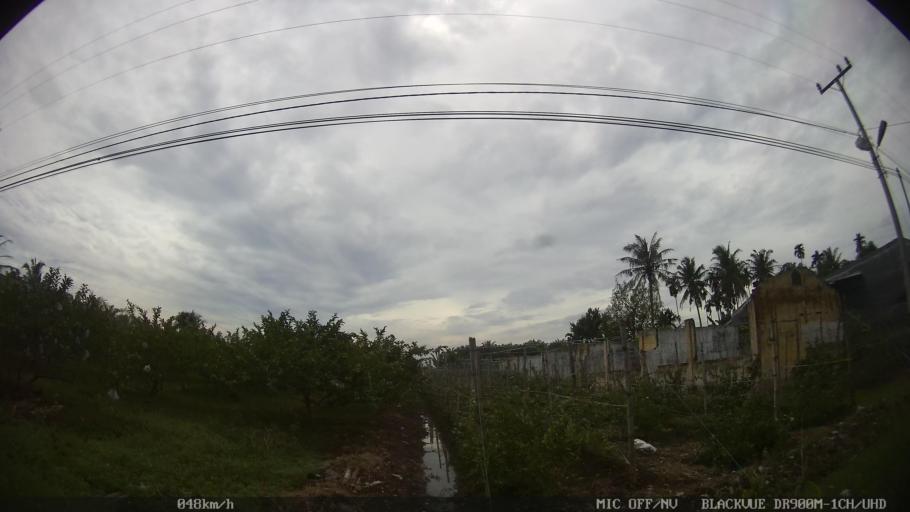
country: ID
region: North Sumatra
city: Sunggal
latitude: 3.5737
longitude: 98.5647
